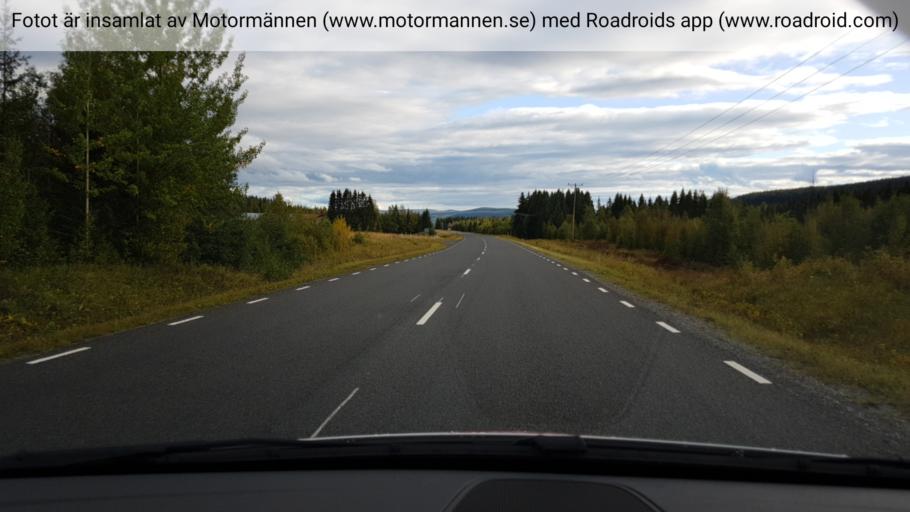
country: SE
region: Jaemtland
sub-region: Are Kommun
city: Jarpen
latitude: 63.3728
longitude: 13.4285
